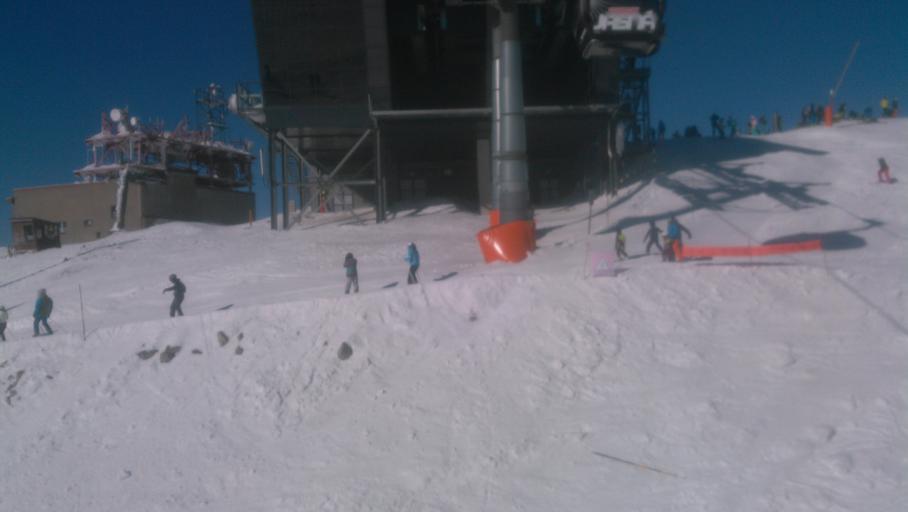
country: SK
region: Zilinsky
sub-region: Okres Liptovsky Mikulas
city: Liptovsky Mikulas
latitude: 48.9430
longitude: 19.5907
